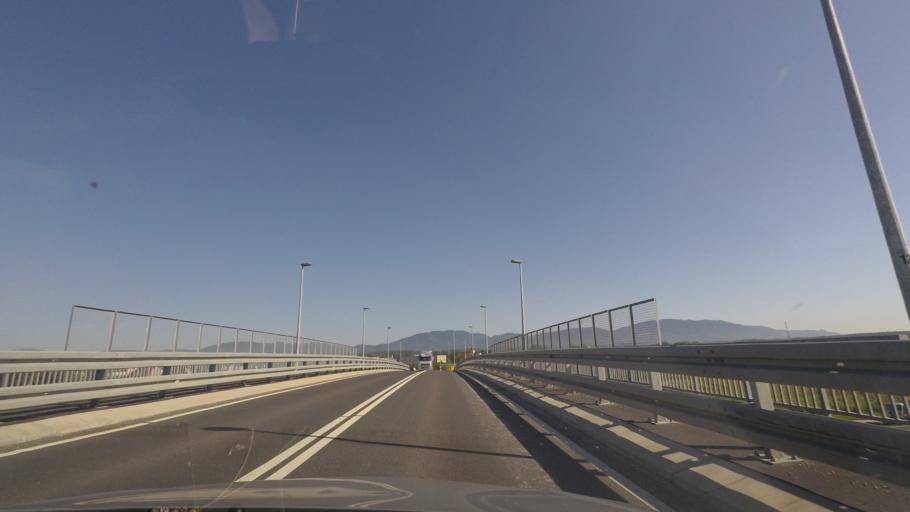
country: HR
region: Zagrebacka
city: Jastrebarsko
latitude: 45.6588
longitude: 15.6531
